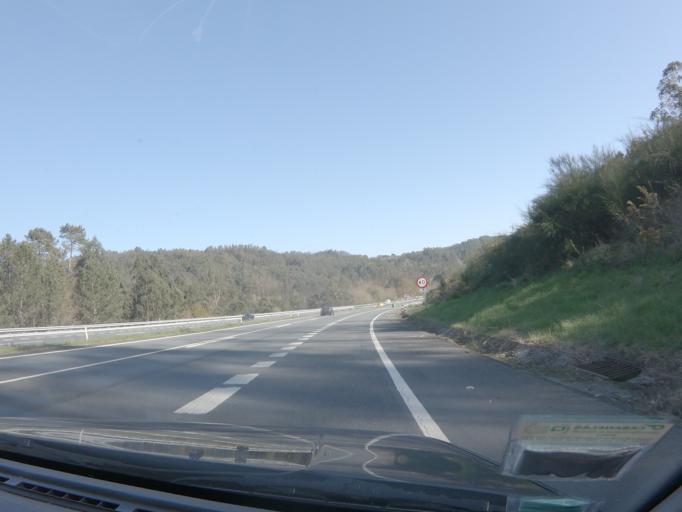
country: ES
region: Galicia
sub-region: Provincia da Coruna
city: Coiros
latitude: 43.2621
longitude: -8.1904
